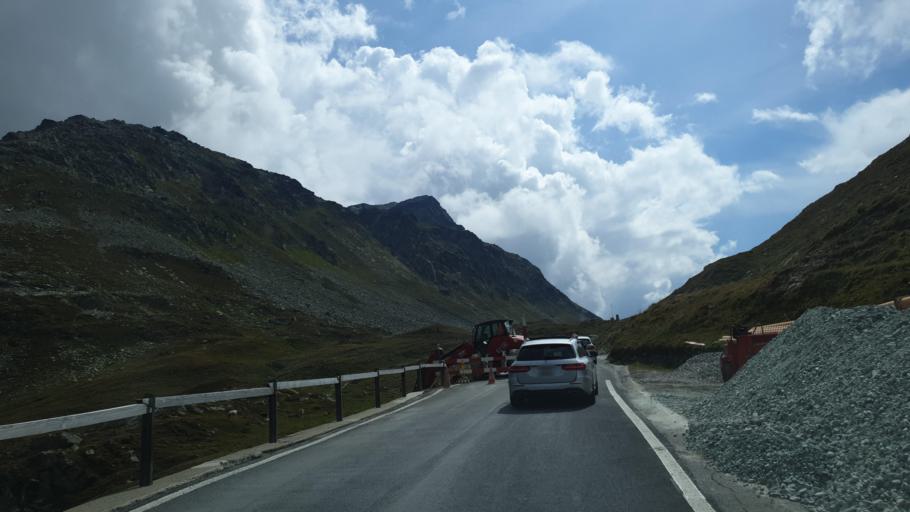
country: IT
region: Lombardy
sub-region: Provincia di Sondrio
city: Campodolcino
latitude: 46.5088
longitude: 9.3290
